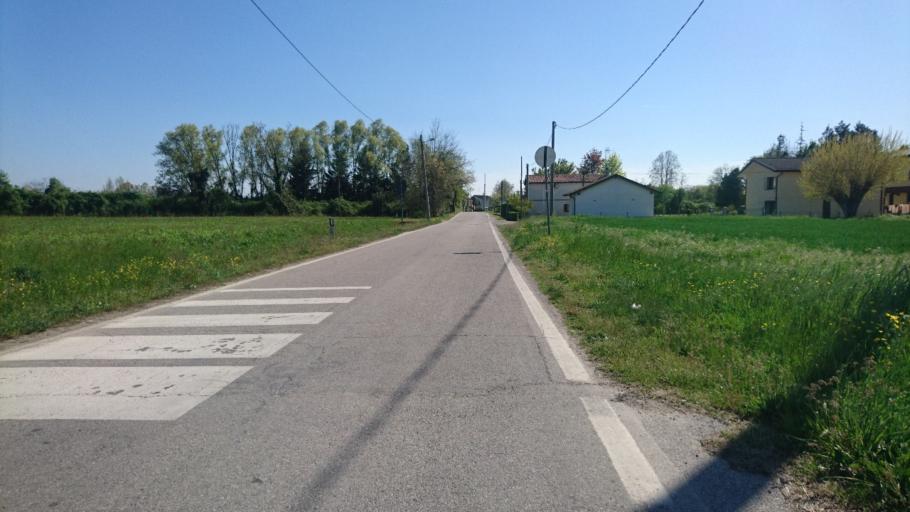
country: IT
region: Veneto
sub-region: Provincia di Venezia
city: Dese
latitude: 45.5204
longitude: 12.2669
